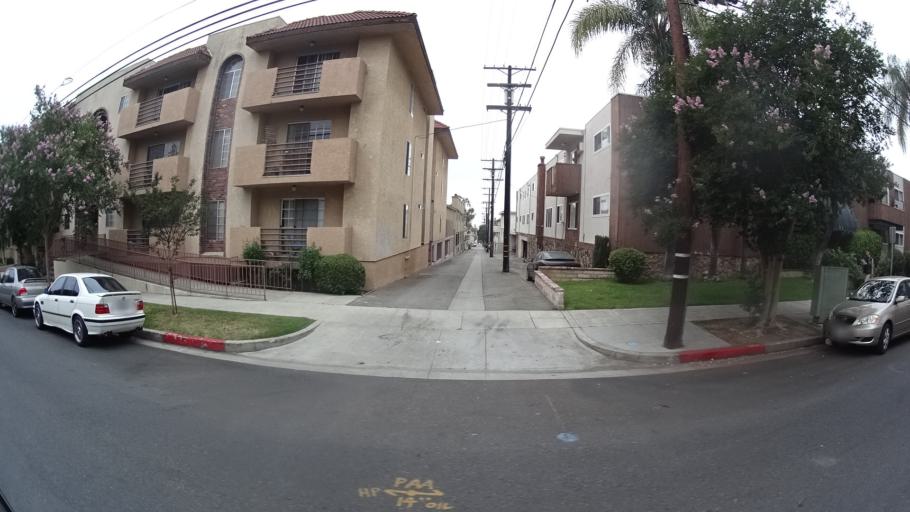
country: US
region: California
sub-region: Los Angeles County
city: Burbank
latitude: 34.1837
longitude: -118.3013
